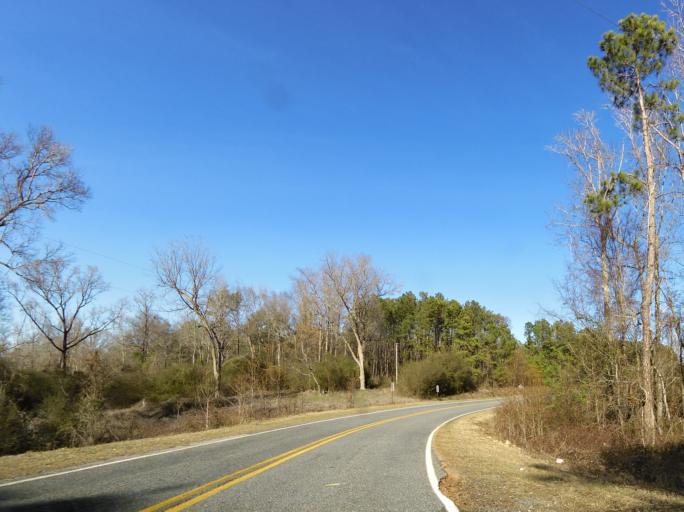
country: US
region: Georgia
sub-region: Crawford County
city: Knoxville
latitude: 32.7241
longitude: -83.9871
